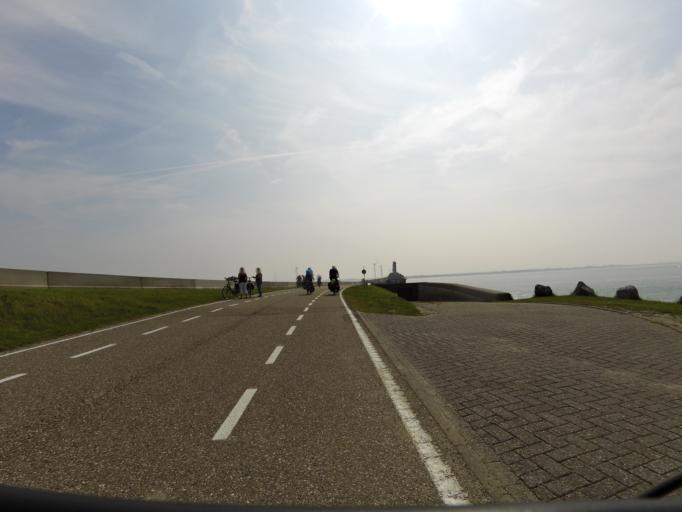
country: NL
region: Zeeland
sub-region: Gemeente Noord-Beveland
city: Kamperland
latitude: 51.6157
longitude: 3.6840
